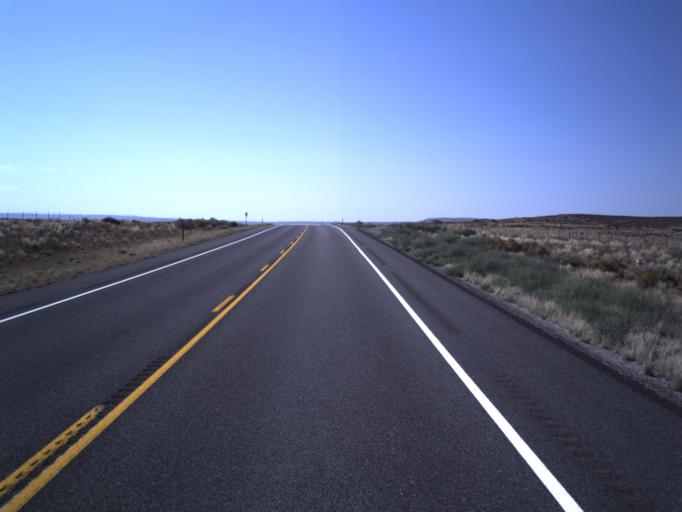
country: US
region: Utah
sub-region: San Juan County
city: Blanding
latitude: 37.3407
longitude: -109.5199
